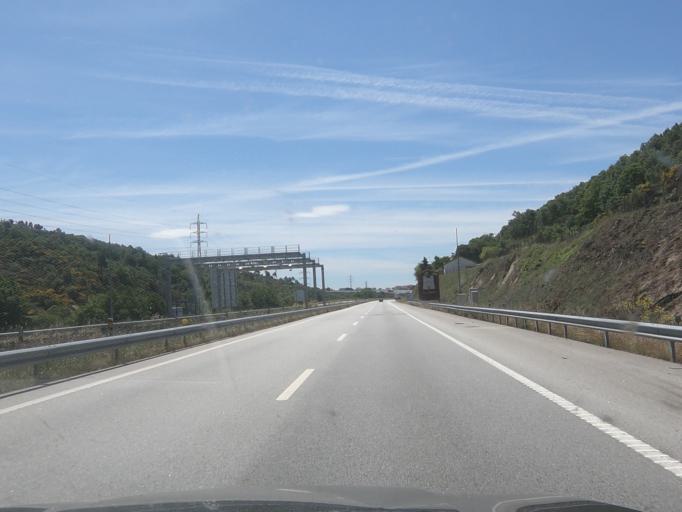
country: PT
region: Guarda
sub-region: Guarda
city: Sequeira
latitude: 40.5779
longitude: -7.2518
